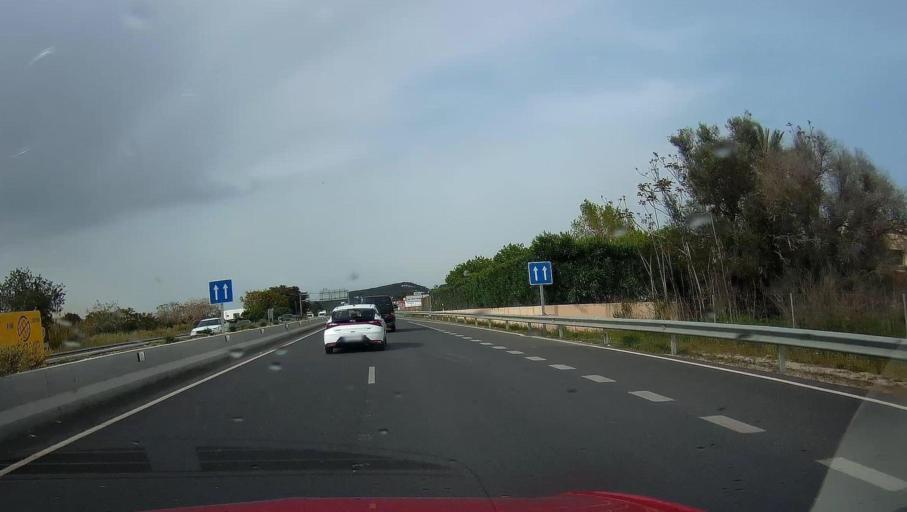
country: ES
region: Balearic Islands
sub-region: Illes Balears
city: Ibiza
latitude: 38.9294
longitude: 1.4426
